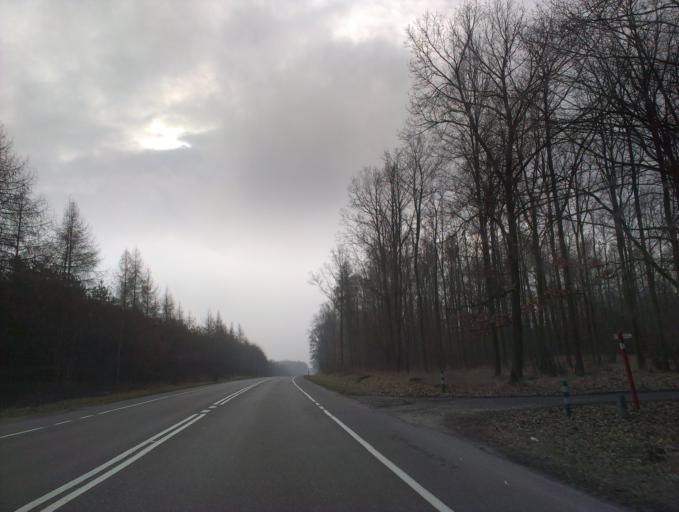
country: PL
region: Greater Poland Voivodeship
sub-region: Powiat chodzieski
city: Budzyn
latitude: 52.9351
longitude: 16.9645
